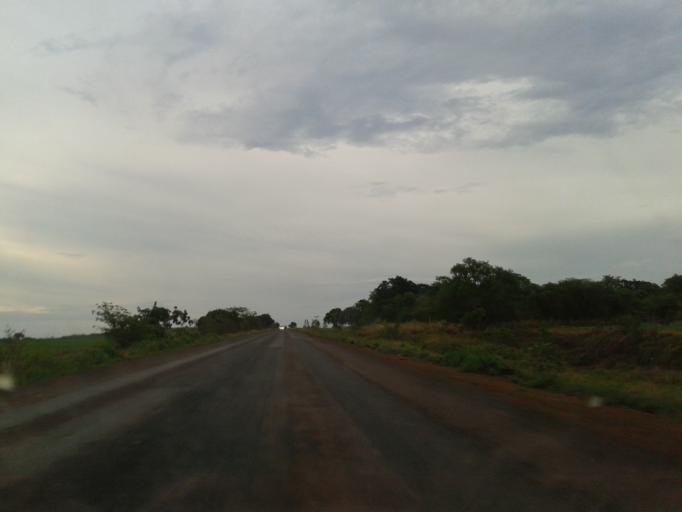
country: BR
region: Goias
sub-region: Santa Helena De Goias
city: Santa Helena de Goias
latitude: -18.0451
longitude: -50.4878
